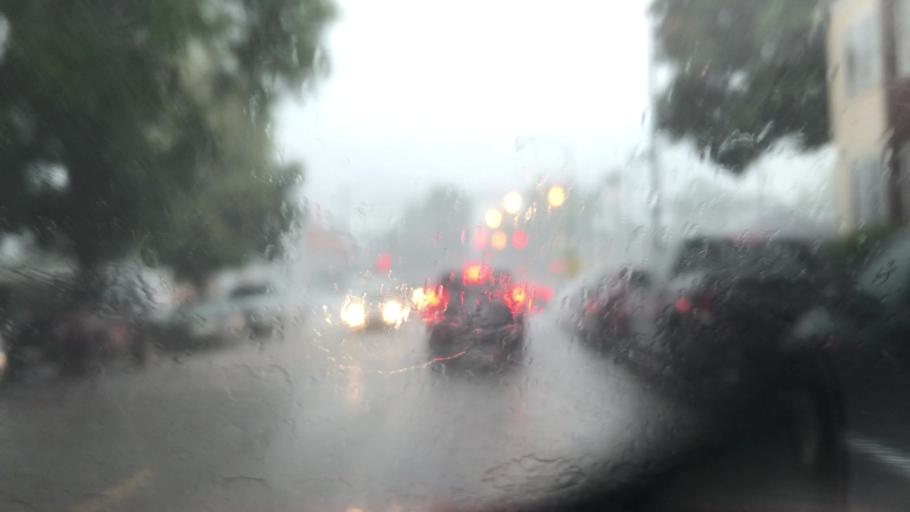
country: US
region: Illinois
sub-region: Cook County
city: Harwood Heights
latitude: 41.9524
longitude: -87.7571
